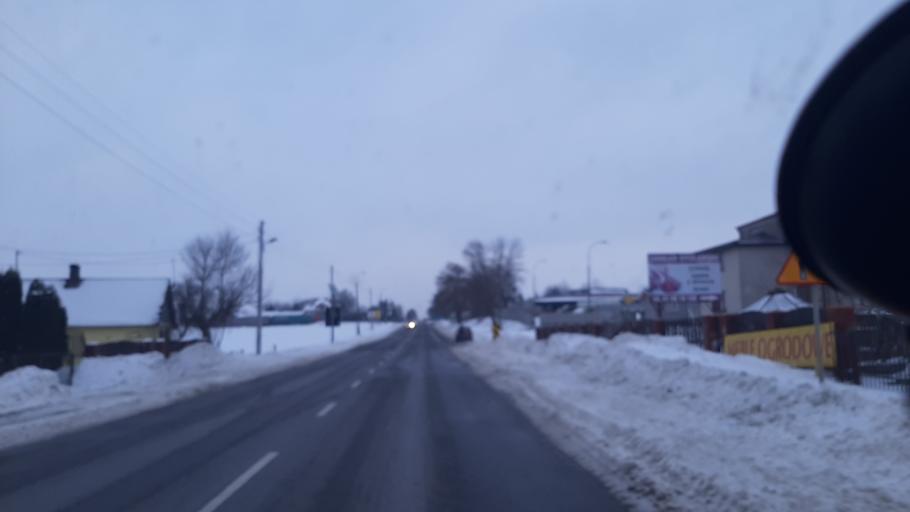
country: PL
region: Lublin Voivodeship
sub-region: Powiat pulawski
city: Markuszow
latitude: 51.3731
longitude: 22.2682
